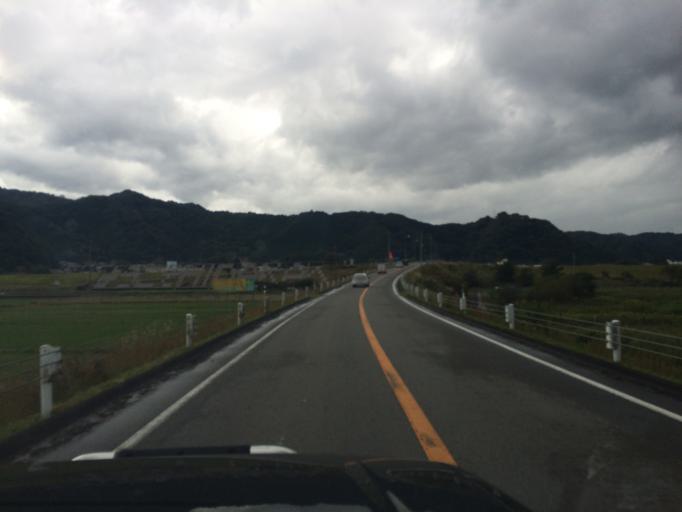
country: JP
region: Hyogo
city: Toyooka
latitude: 35.4518
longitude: 134.7801
